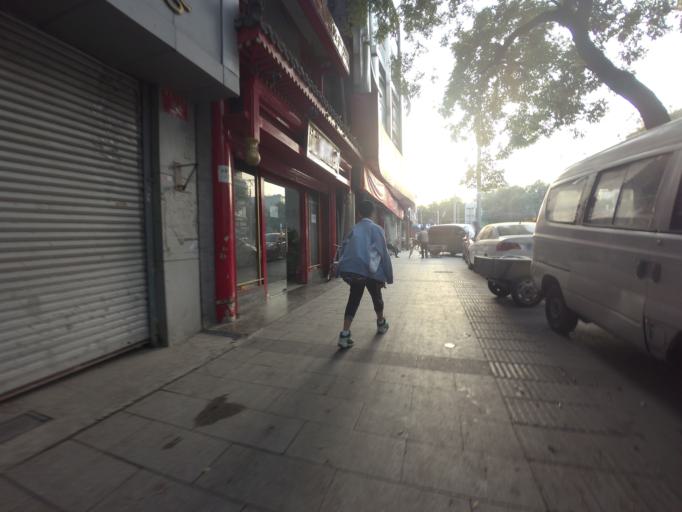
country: CN
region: Beijing
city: Jinrongjie
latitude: 39.9213
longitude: 116.3682
